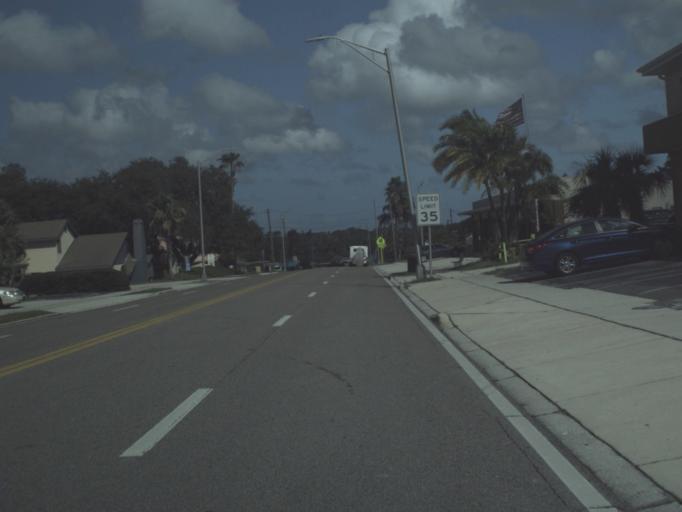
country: US
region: Florida
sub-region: Pinellas County
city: Clearwater
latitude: 27.9631
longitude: -82.7775
